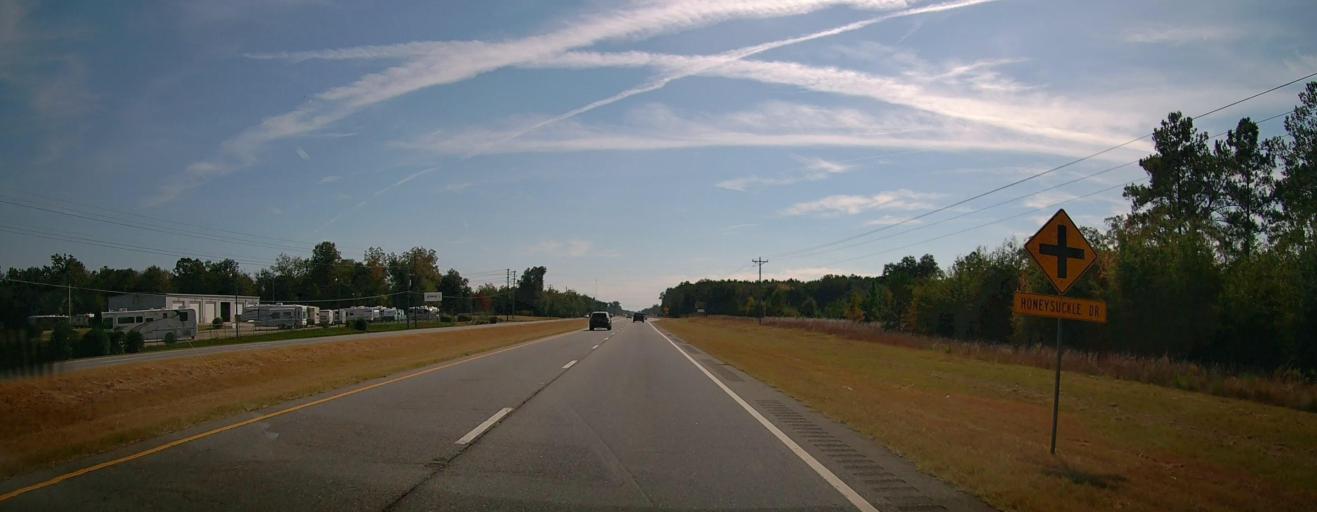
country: US
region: Georgia
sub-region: Dougherty County
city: Putney
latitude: 31.5204
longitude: -84.1157
